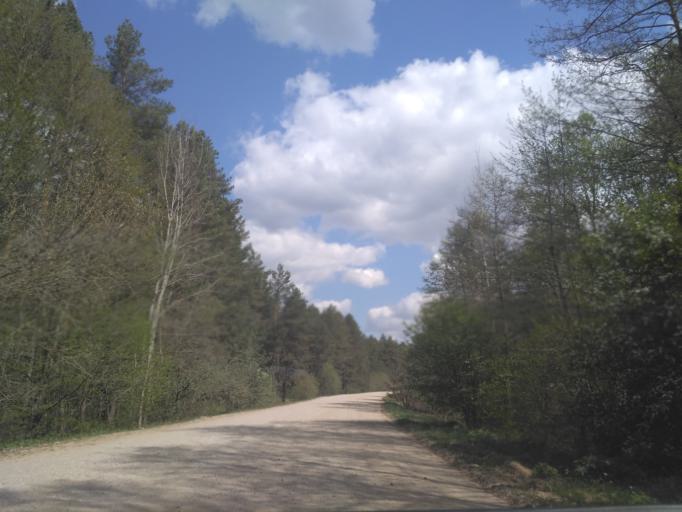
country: BY
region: Minsk
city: Radashkovichy
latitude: 54.2544
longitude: 27.2856
